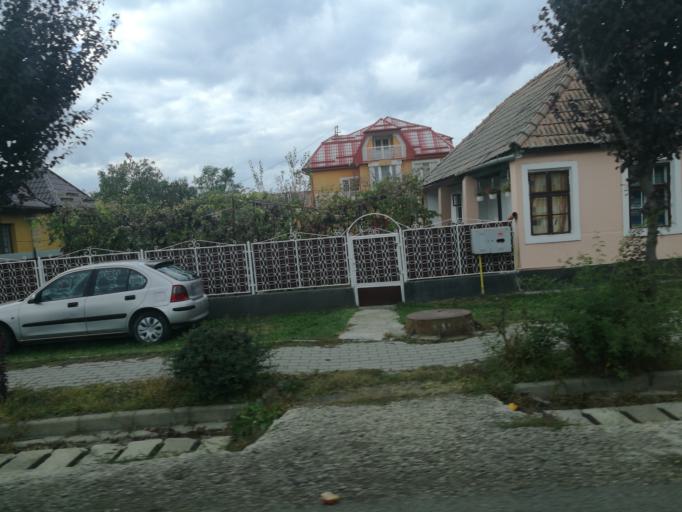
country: RO
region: Mures
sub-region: Comuna Ungheni
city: Ungheni
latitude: 46.4896
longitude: 24.4663
